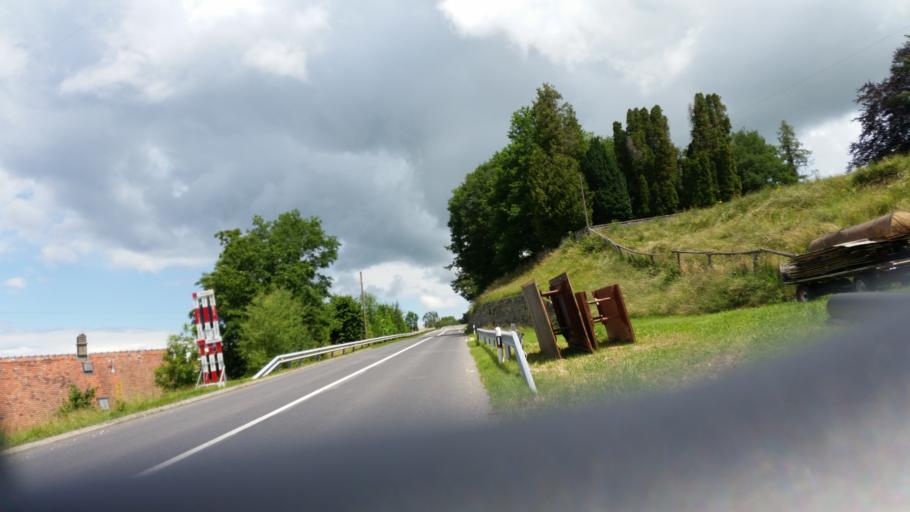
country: CH
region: Vaud
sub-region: Gros-de-Vaud District
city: Rueyres
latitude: 46.7328
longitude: 6.7402
